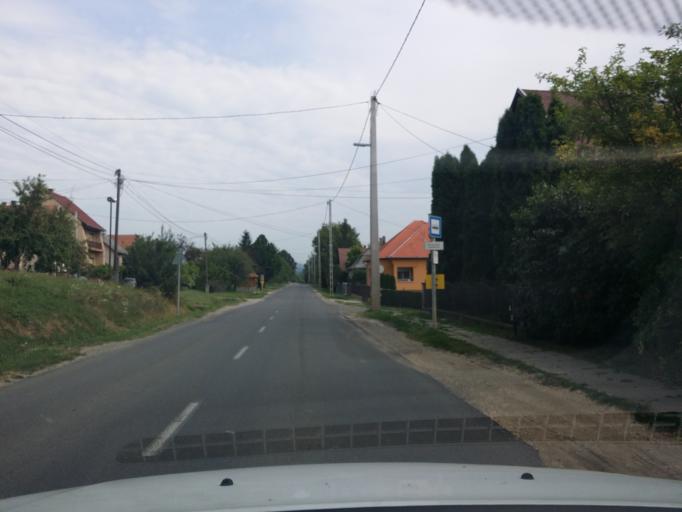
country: HU
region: Pest
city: Acsa
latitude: 47.8008
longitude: 19.3847
